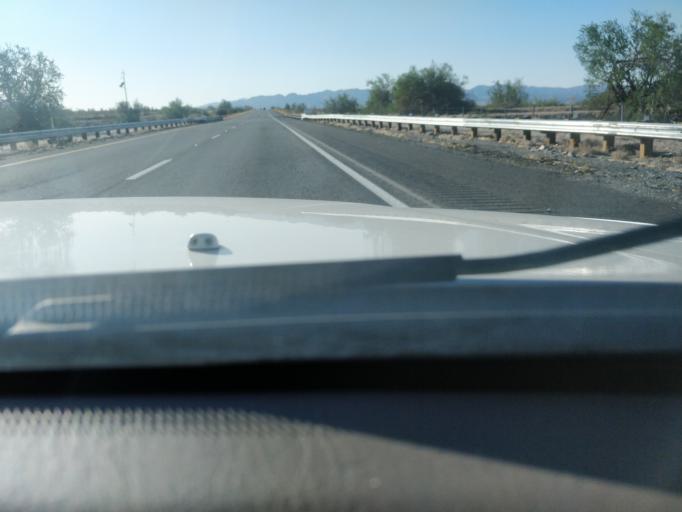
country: US
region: California
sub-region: Imperial County
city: Niland
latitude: 33.7042
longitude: -115.3276
